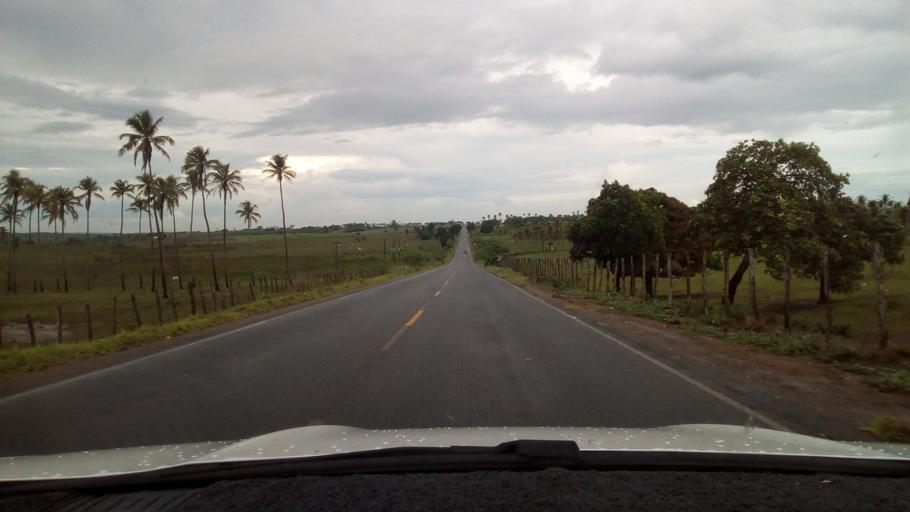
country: BR
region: Paraiba
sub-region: Mari
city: Mari
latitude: -7.0619
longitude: -35.2977
